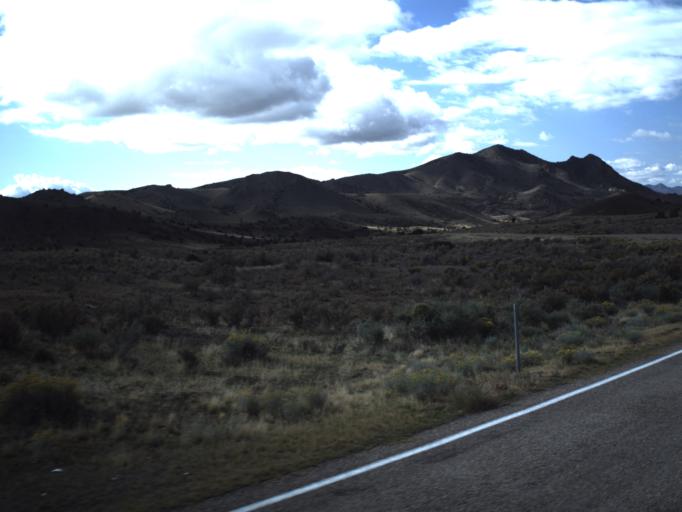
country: US
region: Utah
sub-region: Beaver County
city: Milford
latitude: 38.4568
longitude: -113.2579
